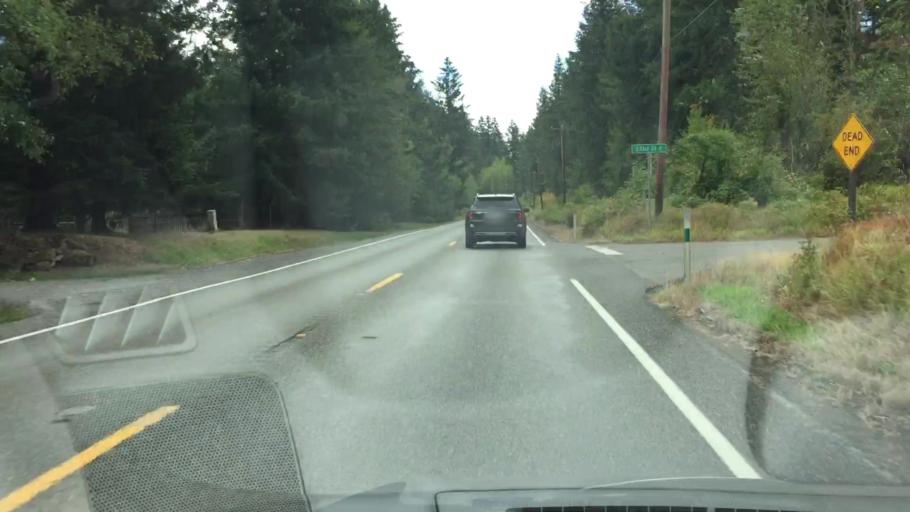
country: US
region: Washington
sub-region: Pierce County
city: Eatonville
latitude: 46.9105
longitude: -122.2954
